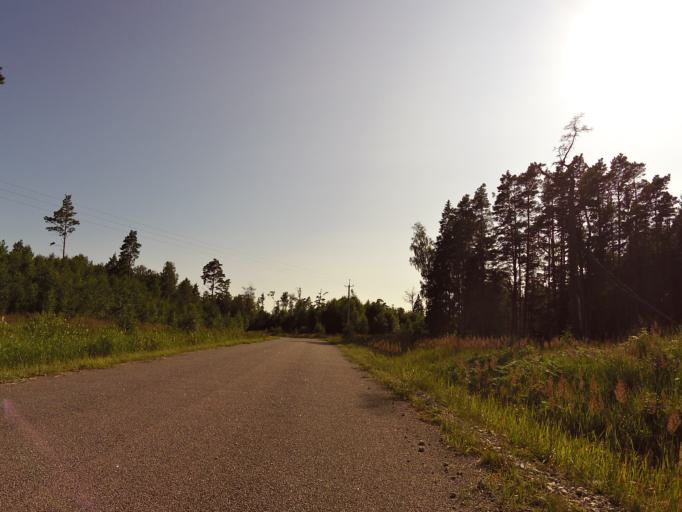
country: EE
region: Hiiumaa
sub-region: Kaerdla linn
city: Kardla
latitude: 58.9022
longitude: 22.2810
